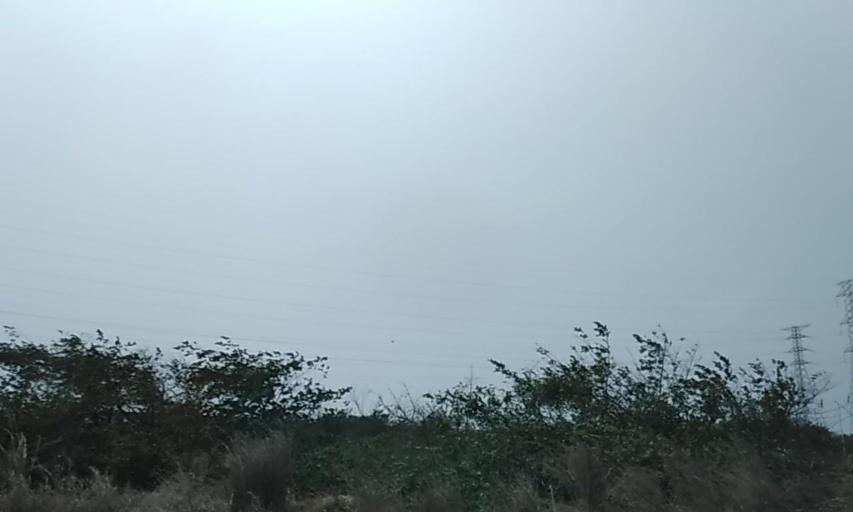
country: MX
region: Veracruz
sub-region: Veracruz
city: Las Amapolas
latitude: 19.1759
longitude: -96.1920
